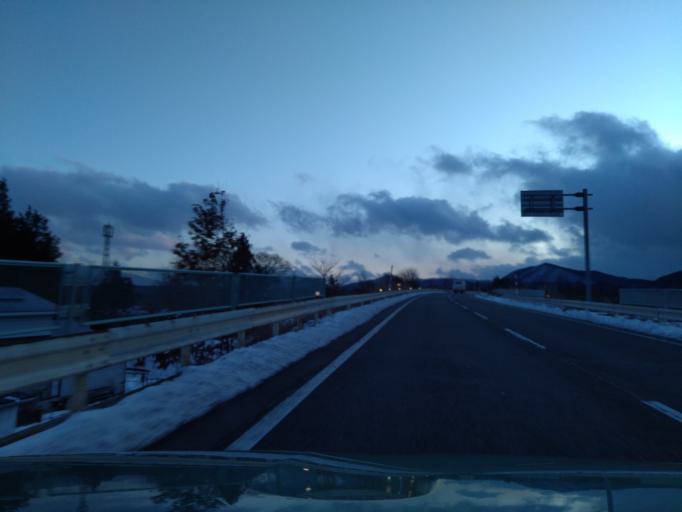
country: JP
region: Iwate
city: Shizukuishi
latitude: 39.6952
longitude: 140.9363
